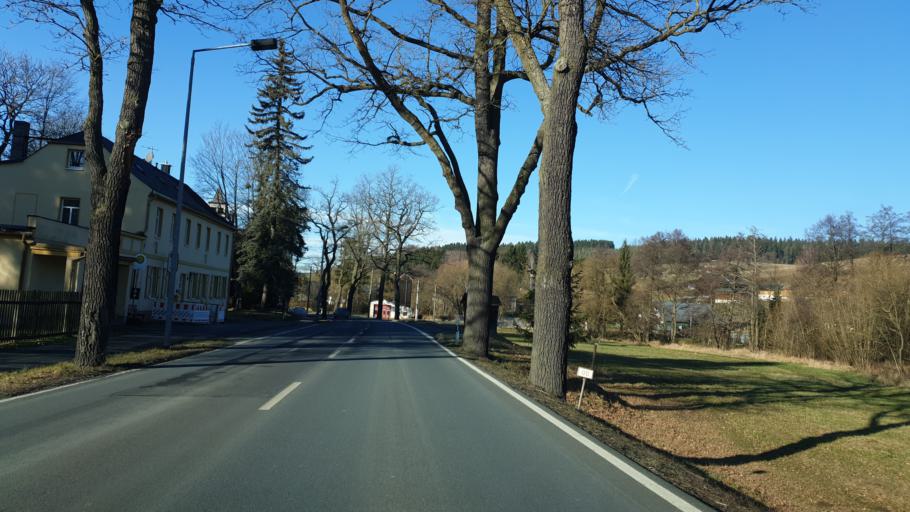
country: DE
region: Saxony
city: Adorf
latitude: 50.2931
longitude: 12.2686
